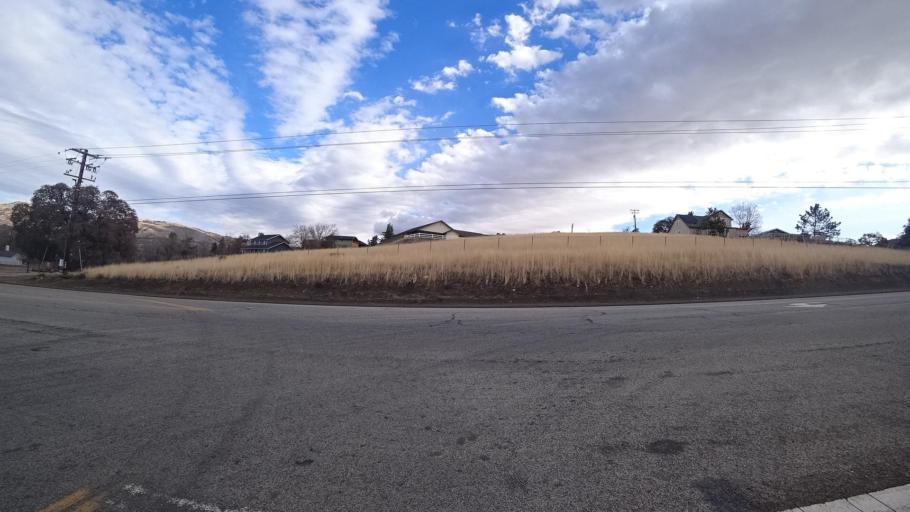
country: US
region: California
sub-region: Kern County
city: Golden Hills
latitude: 35.1425
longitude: -118.4949
